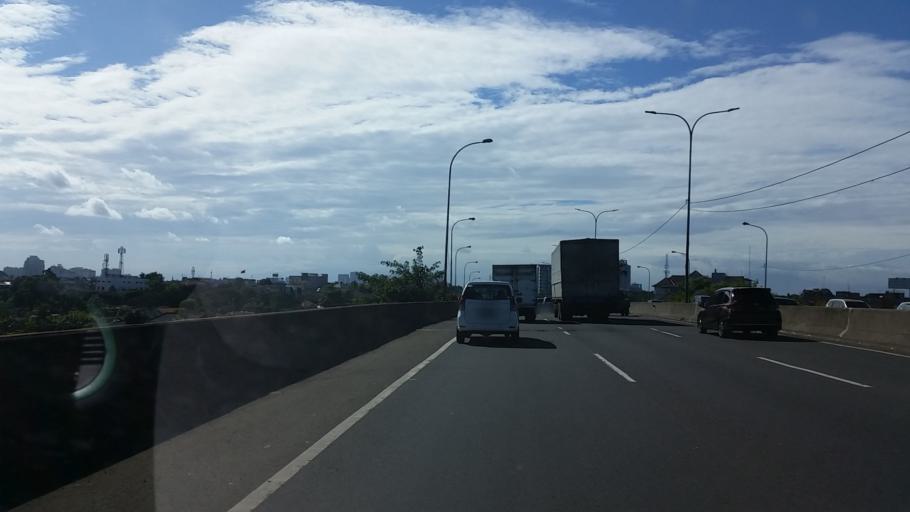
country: ID
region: Banten
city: South Tangerang
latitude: -6.2552
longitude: 106.7649
